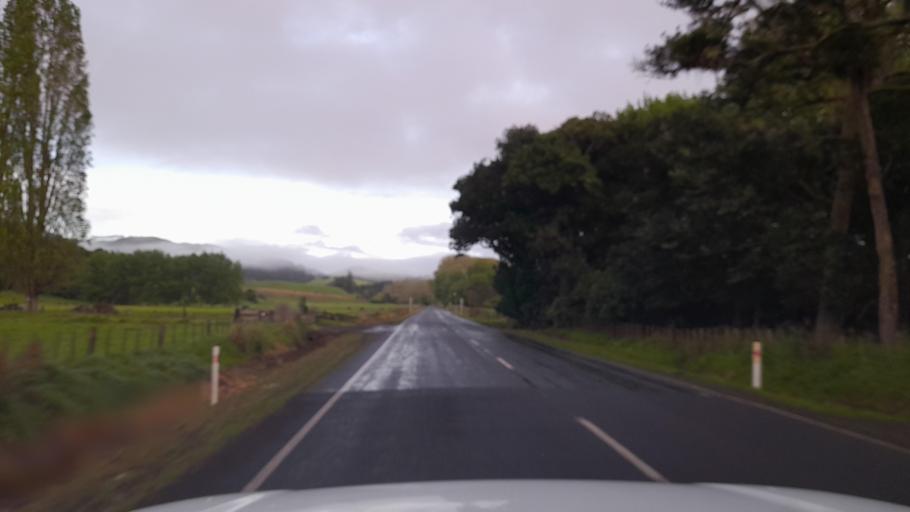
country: NZ
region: Northland
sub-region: Kaipara District
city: Dargaville
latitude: -35.7010
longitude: 173.9244
